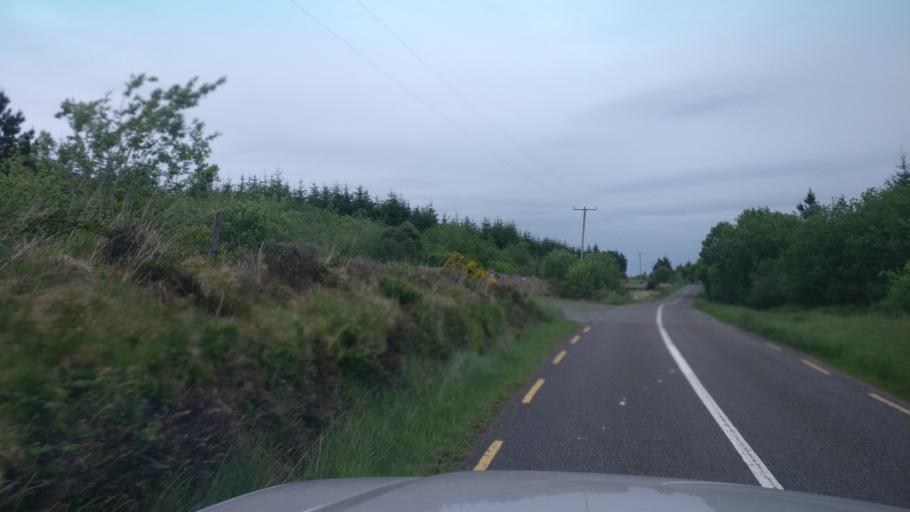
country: IE
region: Connaught
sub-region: County Galway
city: Loughrea
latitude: 53.0737
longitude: -8.5740
